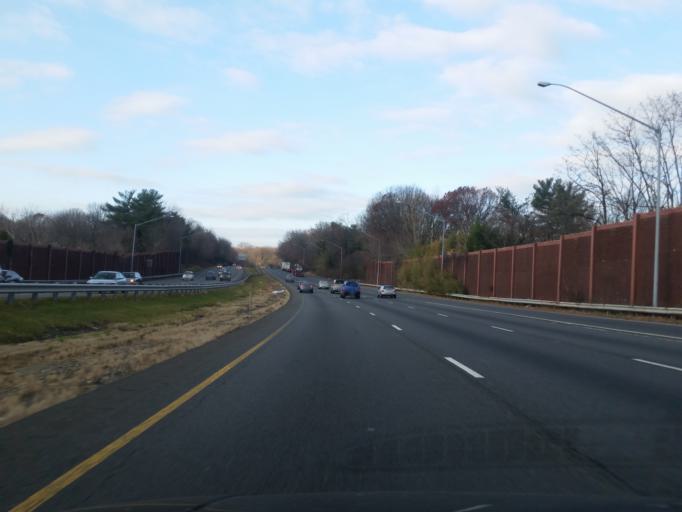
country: US
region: Maryland
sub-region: Montgomery County
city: North Bethesda
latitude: 39.0155
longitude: -77.1222
